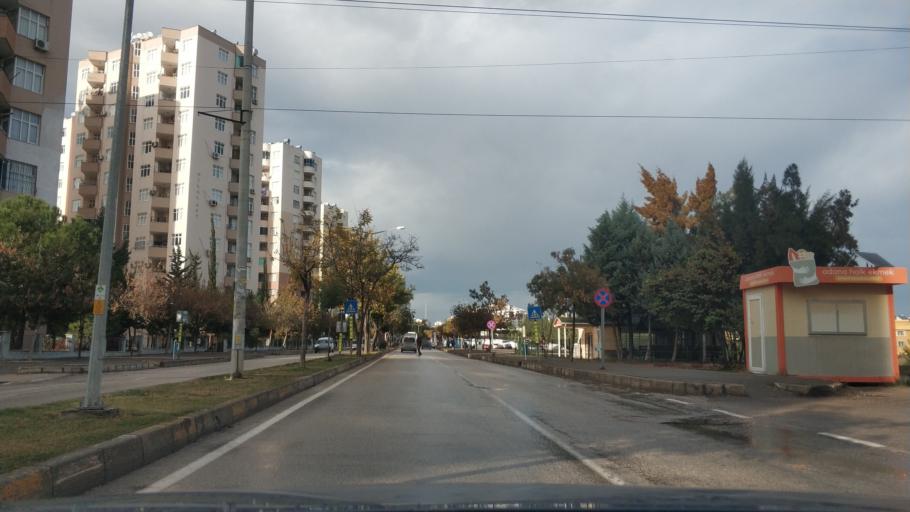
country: TR
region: Adana
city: Seyhan
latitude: 37.0384
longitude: 35.2614
